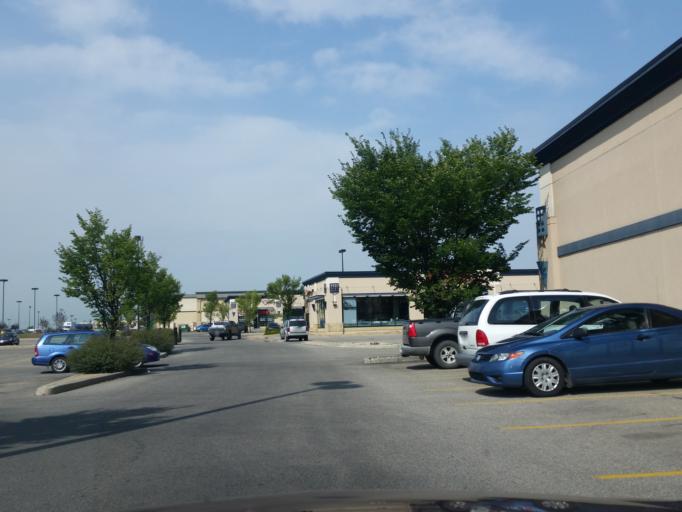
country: CA
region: Alberta
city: Calgary
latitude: 51.0687
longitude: -113.9905
